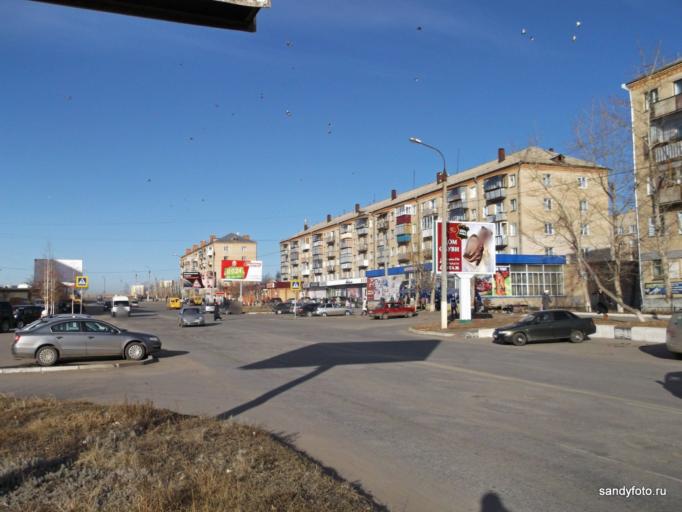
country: RU
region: Chelyabinsk
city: Troitsk
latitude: 54.0778
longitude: 61.5304
